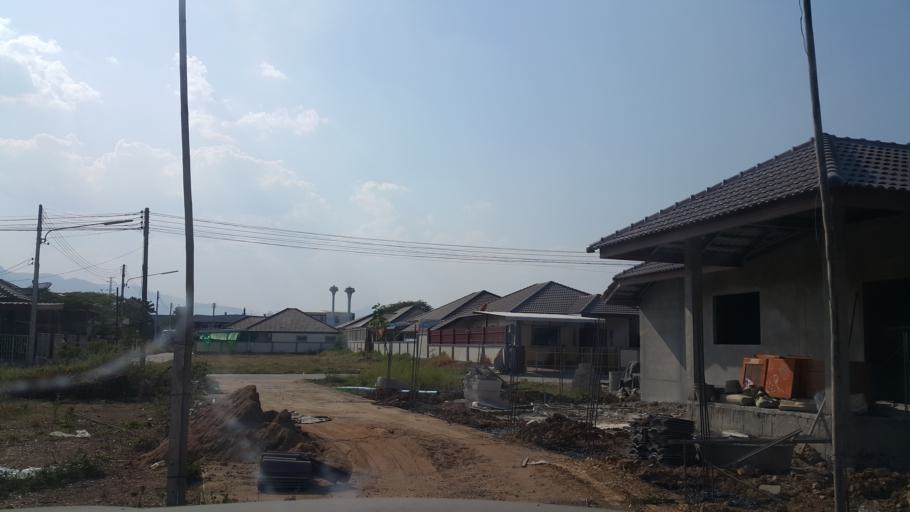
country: TH
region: Chiang Mai
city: San Sai
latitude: 18.8579
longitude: 99.0200
